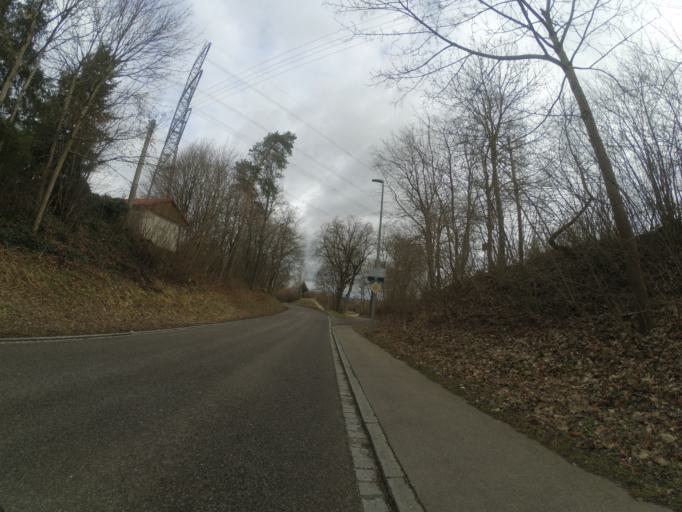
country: DE
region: Bavaria
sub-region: Swabia
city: Bellenberg
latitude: 48.2554
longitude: 10.1245
